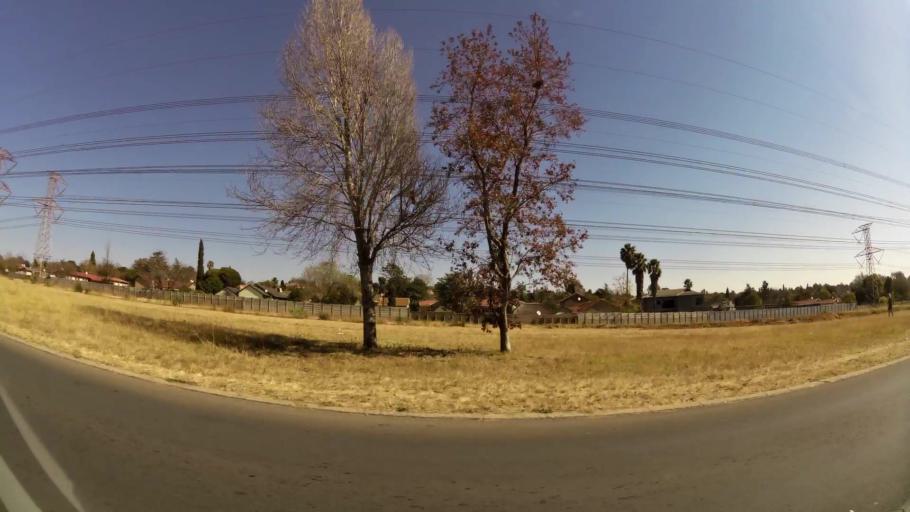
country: ZA
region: Gauteng
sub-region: City of Johannesburg Metropolitan Municipality
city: Modderfontein
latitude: -26.0578
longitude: 28.2145
